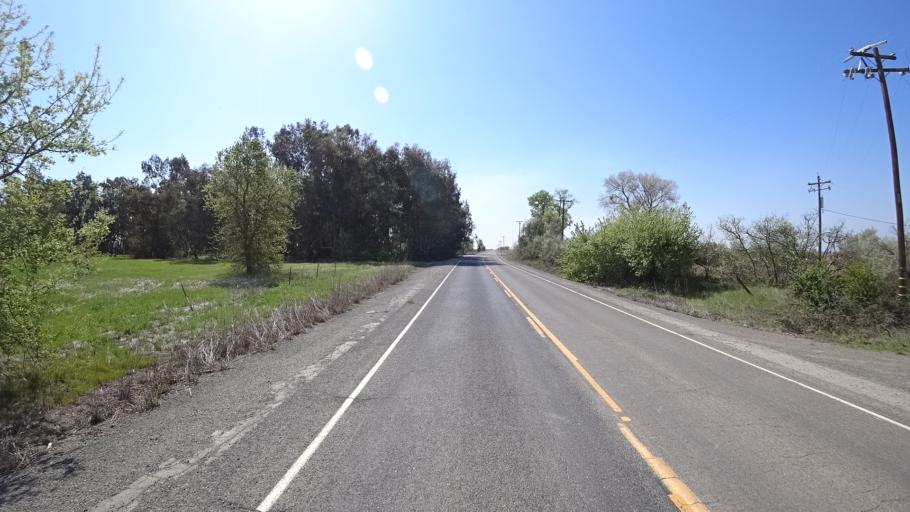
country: US
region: California
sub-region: Butte County
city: Durham
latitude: 39.5456
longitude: -121.9085
